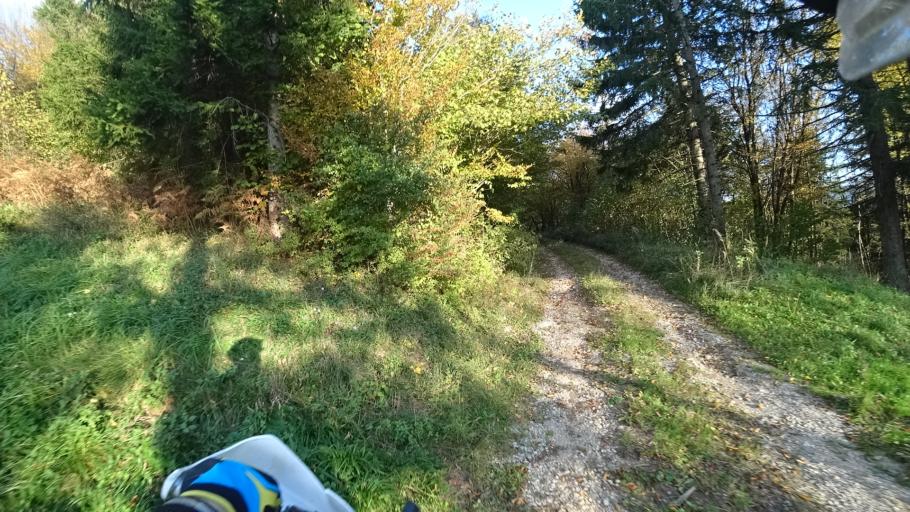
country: HR
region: Karlovacka
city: Plaski
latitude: 45.0120
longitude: 15.4222
